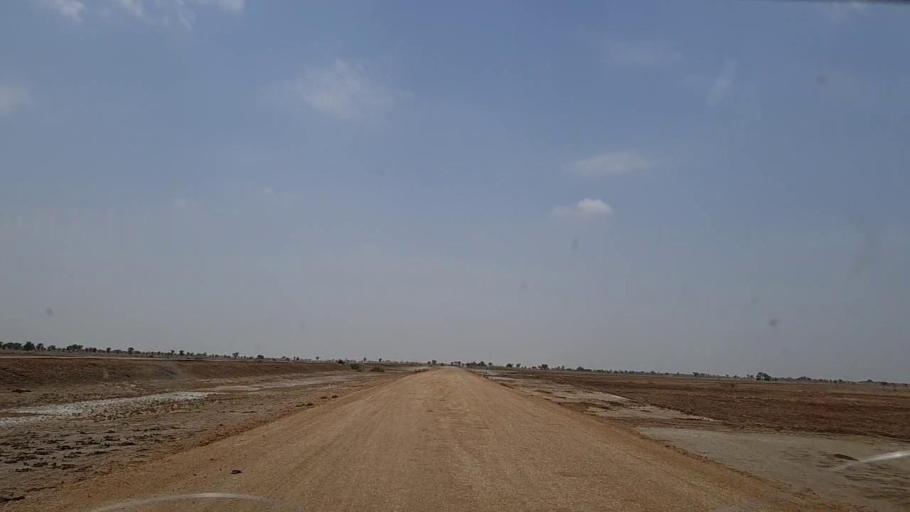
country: PK
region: Sindh
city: Phulji
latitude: 26.7957
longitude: 67.6393
